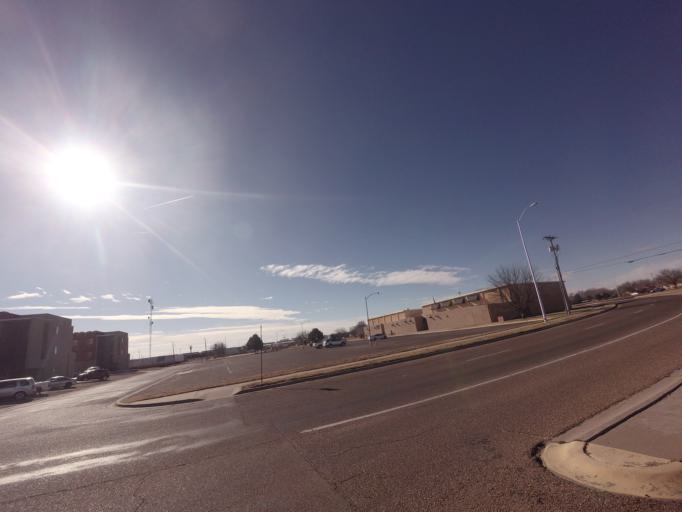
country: US
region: New Mexico
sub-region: Curry County
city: Clovis
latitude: 34.4008
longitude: -103.2093
